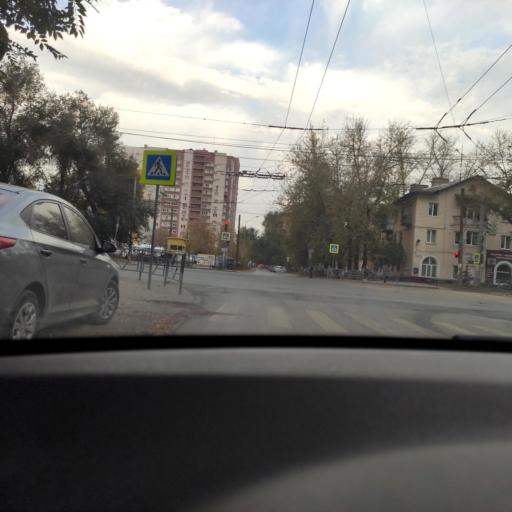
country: RU
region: Samara
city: Samara
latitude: 53.2207
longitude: 50.2471
